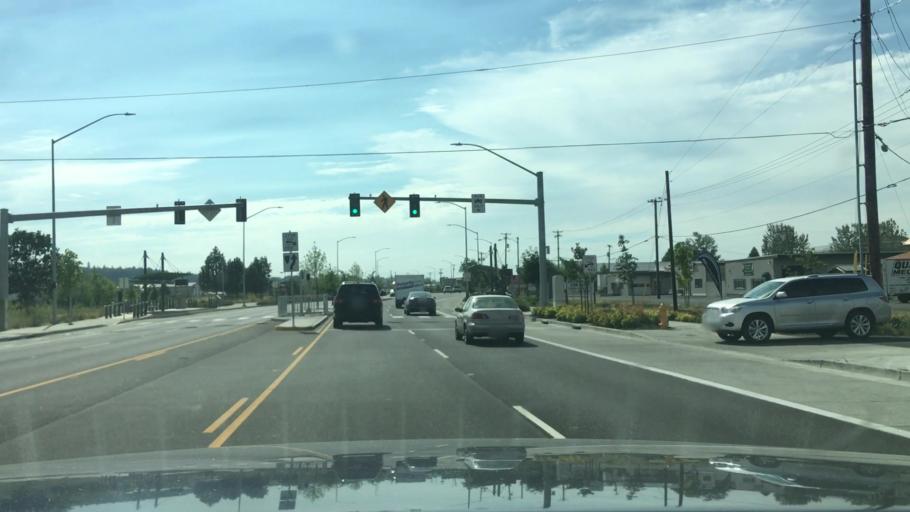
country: US
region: Oregon
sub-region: Lane County
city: Eugene
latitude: 44.0481
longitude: -123.1554
